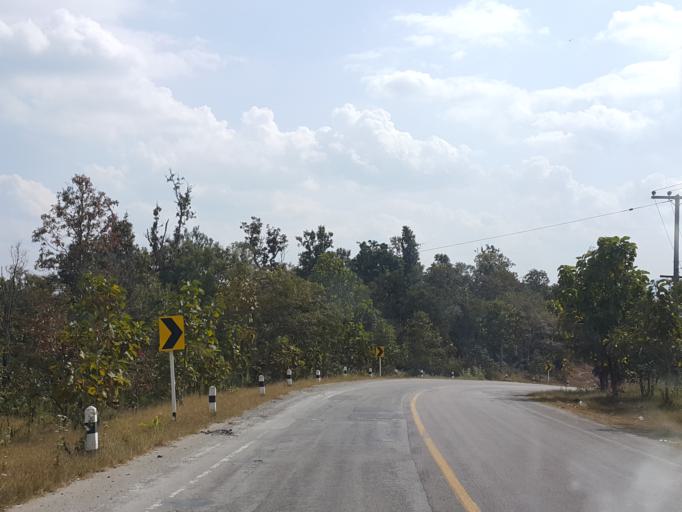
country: TH
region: Chiang Mai
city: Om Koi
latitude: 17.8174
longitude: 98.3679
